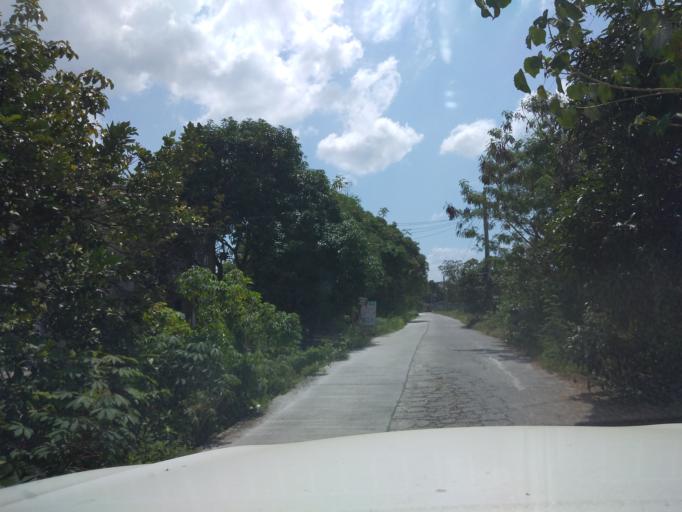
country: PH
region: Central Luzon
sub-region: Province of Pampanga
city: Lourdes
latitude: 15.0112
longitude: 120.8675
